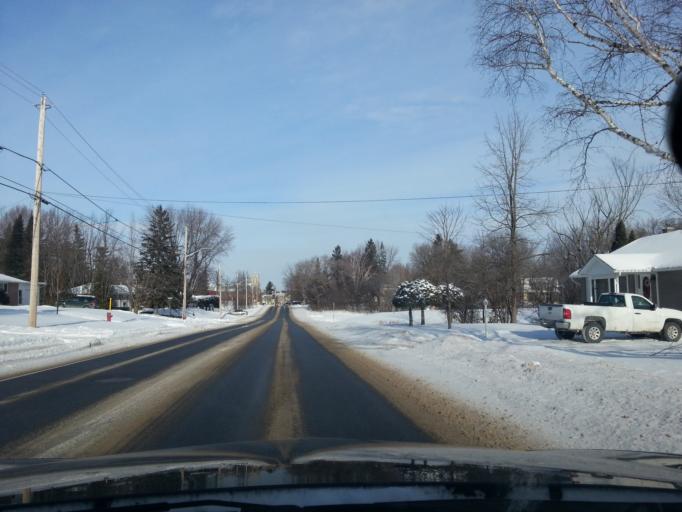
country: CA
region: Ontario
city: Carleton Place
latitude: 45.2192
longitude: -76.1963
